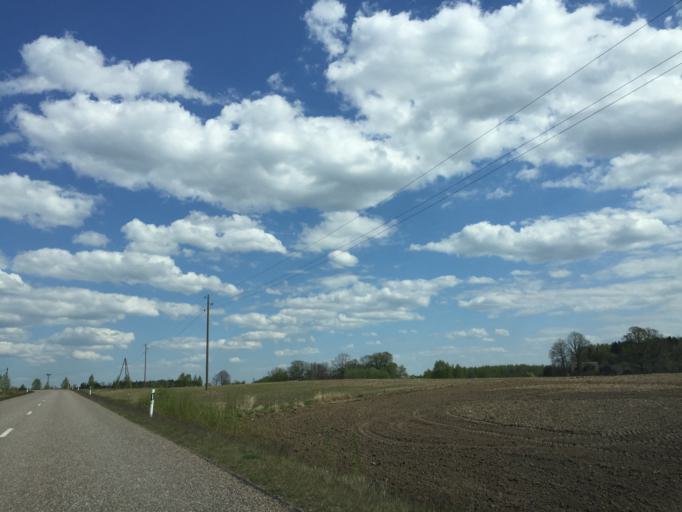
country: LV
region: Saulkrastu
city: Saulkrasti
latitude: 57.3553
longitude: 24.4802
